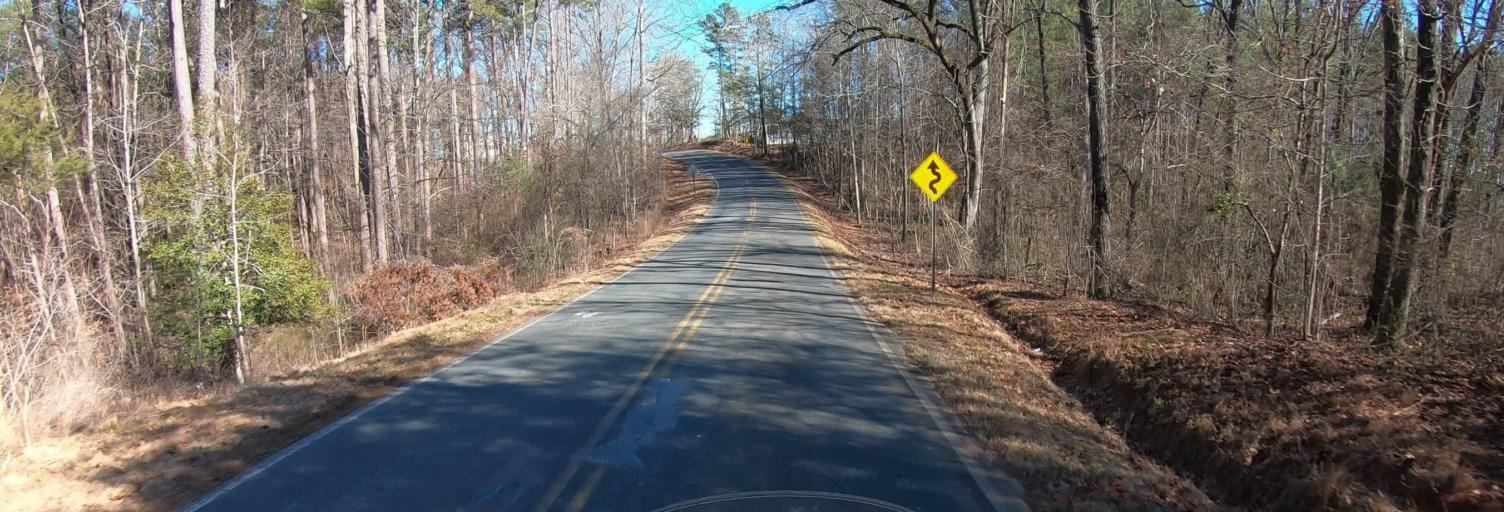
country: US
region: South Carolina
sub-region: Oconee County
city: Walhalla
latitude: 34.7176
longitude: -83.0663
